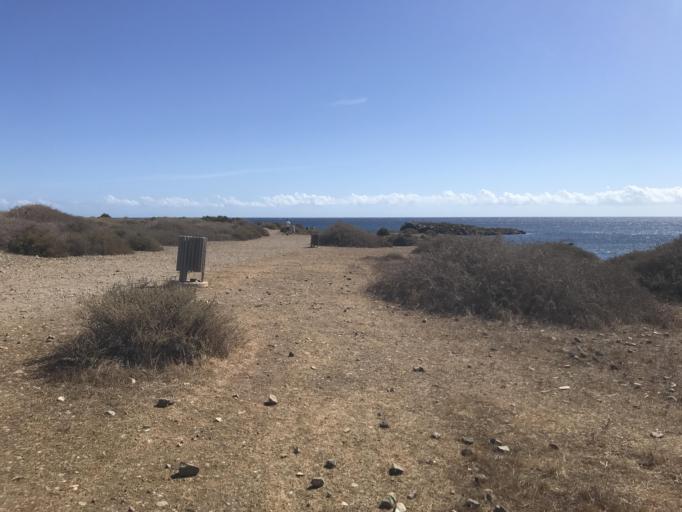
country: ES
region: Valencia
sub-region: Provincia de Alicante
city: Santa Pola
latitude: 38.1640
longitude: -0.4768
